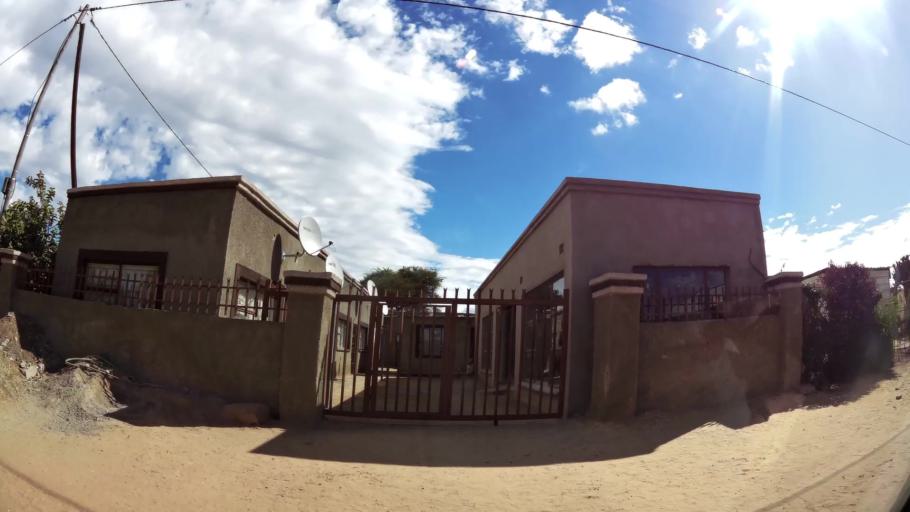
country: ZA
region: Limpopo
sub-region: Waterberg District Municipality
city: Bela-Bela
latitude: -24.8781
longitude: 28.3228
